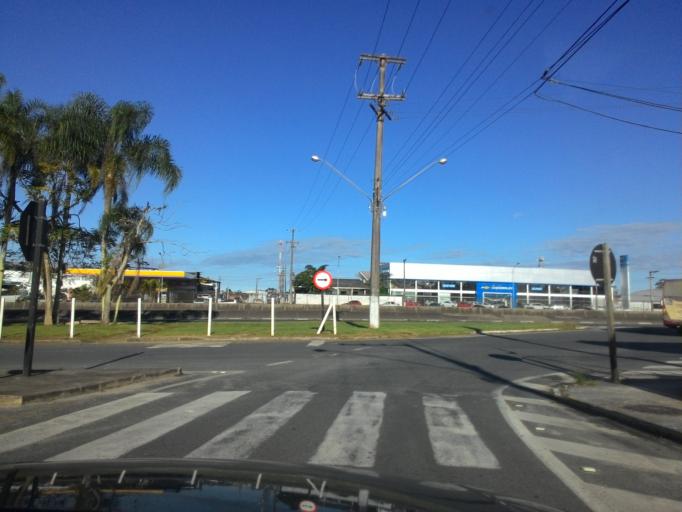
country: BR
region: Sao Paulo
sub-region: Registro
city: Registro
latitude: -24.5008
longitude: -47.8468
